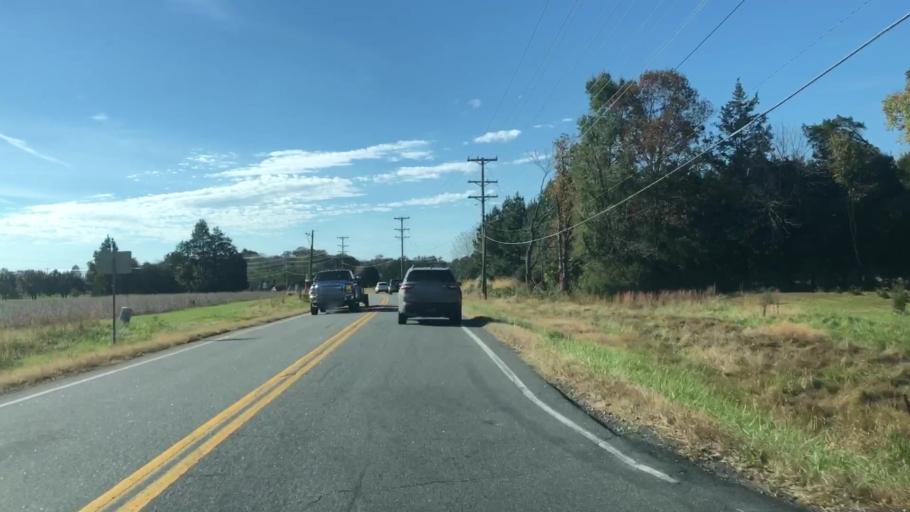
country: US
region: Virginia
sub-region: Prince William County
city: Gainesville
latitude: 38.7534
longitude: -77.6367
